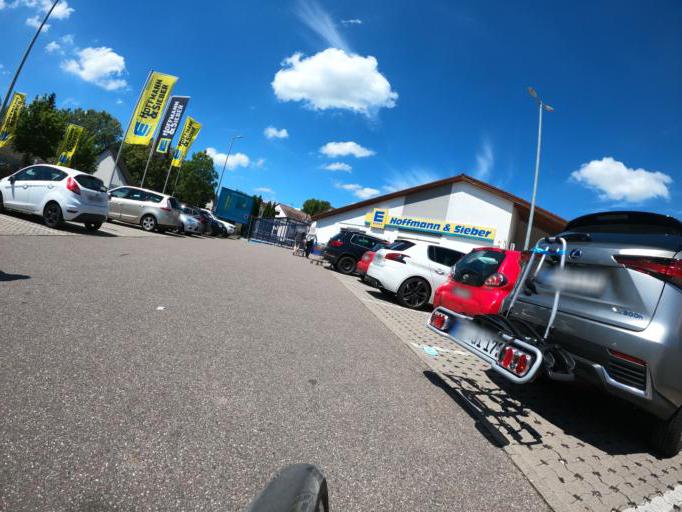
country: DE
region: Baden-Wuerttemberg
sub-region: Regierungsbezirk Stuttgart
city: Sersheim
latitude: 48.9637
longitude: 9.0555
